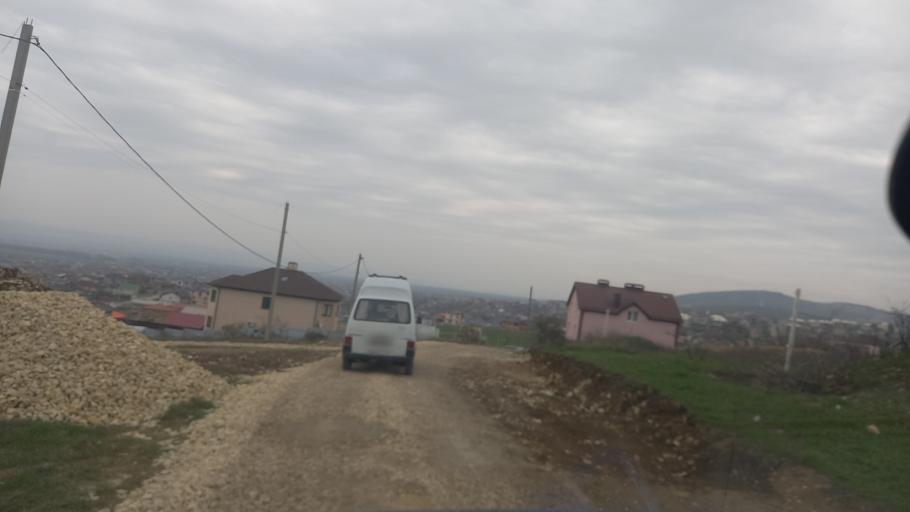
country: RU
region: Krasnodarskiy
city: Anapa
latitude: 44.8569
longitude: 37.3432
